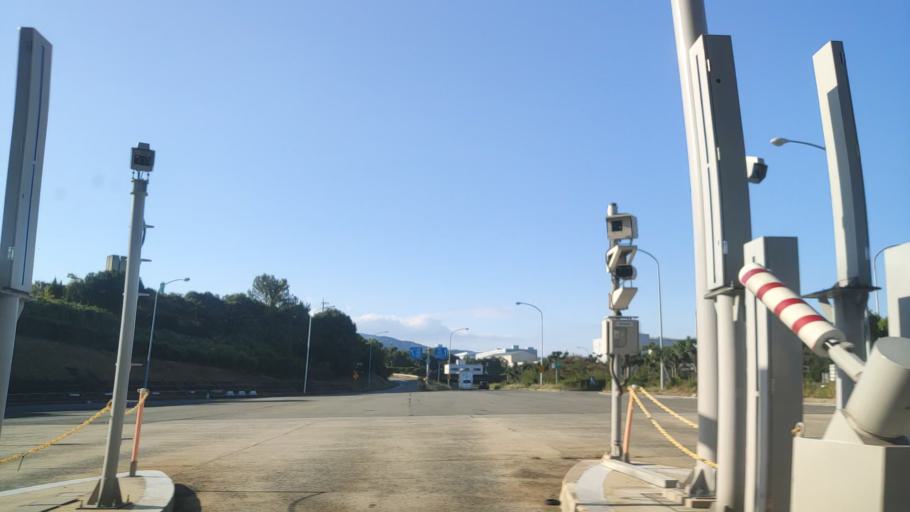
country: JP
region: Hyogo
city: Sandacho
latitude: 34.8362
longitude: 135.2353
